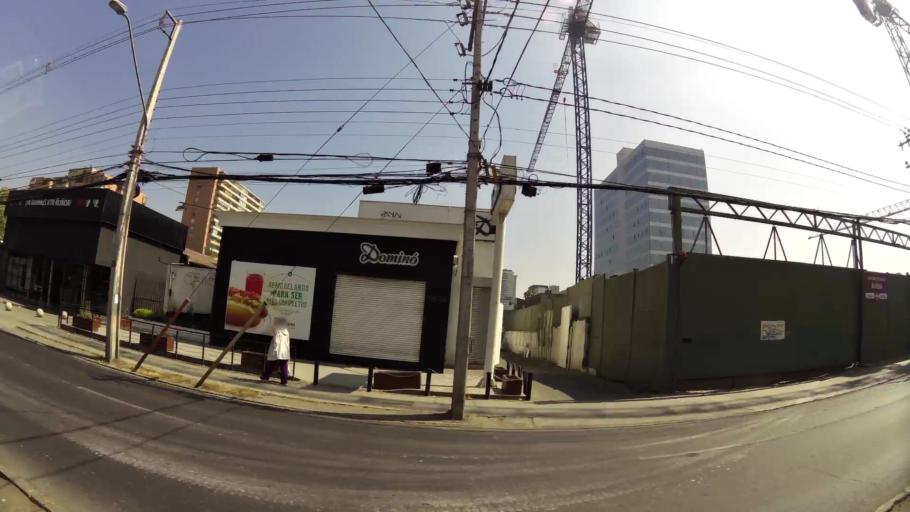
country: CL
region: Santiago Metropolitan
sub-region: Provincia de Santiago
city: Villa Presidente Frei, Nunoa, Santiago, Chile
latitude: -33.4551
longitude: -70.6051
